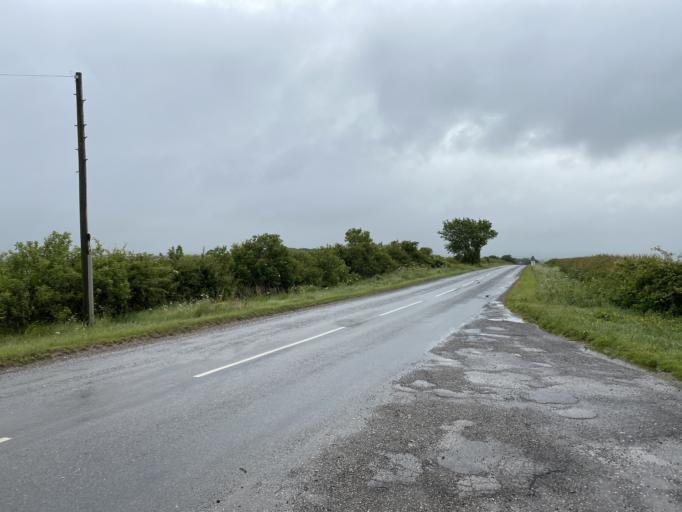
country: GB
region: England
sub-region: East Riding of Yorkshire
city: Wetwang
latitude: 54.0437
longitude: -0.5392
